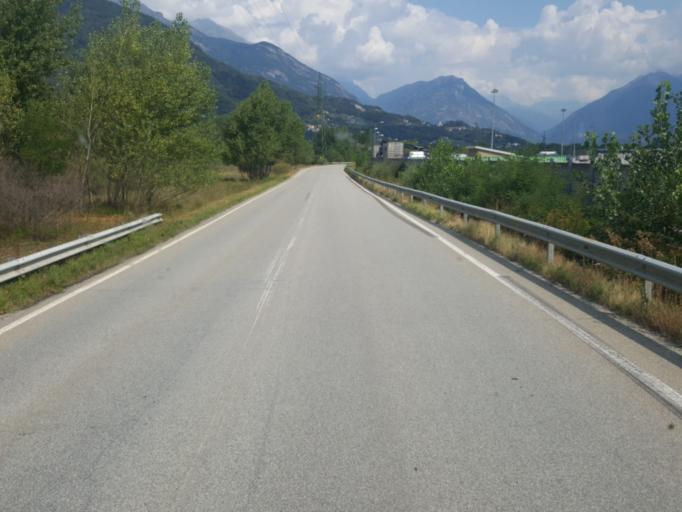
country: IT
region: Piedmont
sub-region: Provincia Verbano-Cusio-Ossola
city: Beura
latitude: 46.0727
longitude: 8.2849
